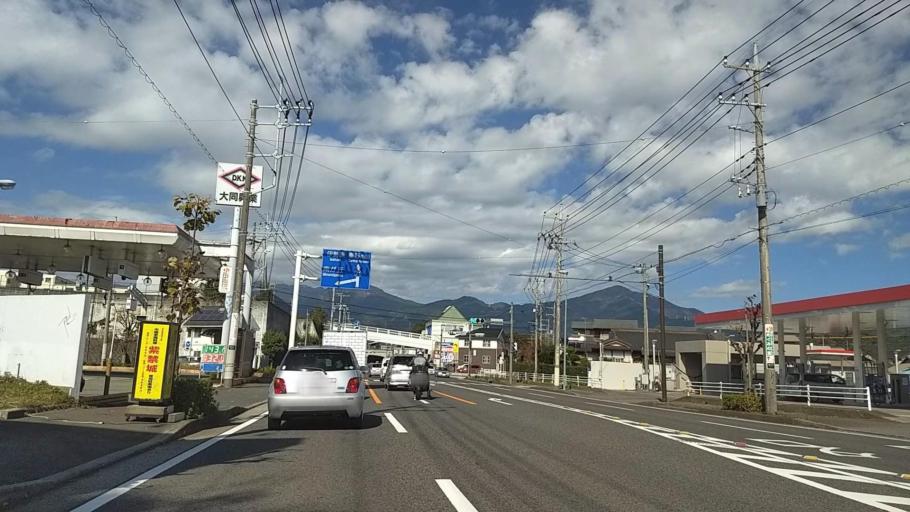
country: JP
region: Kanagawa
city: Hadano
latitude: 35.3566
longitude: 139.2357
